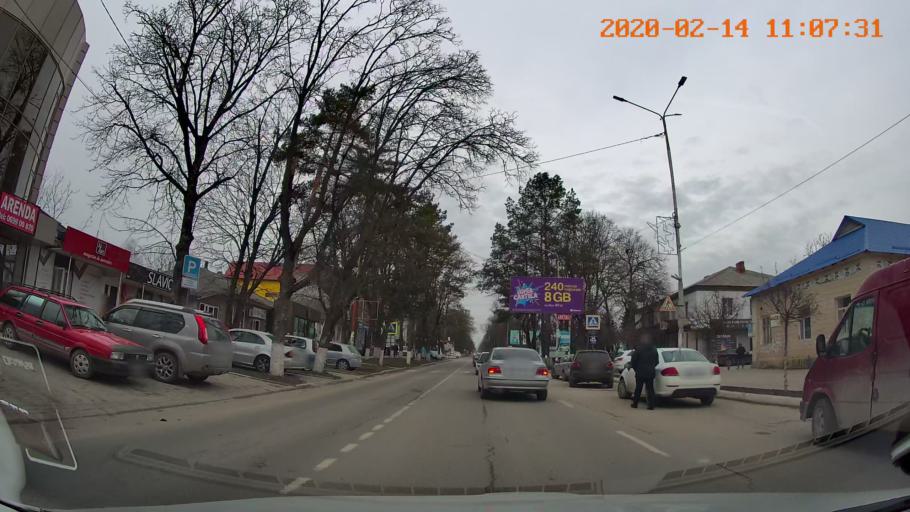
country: MD
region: Raionul Edinet
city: Edinet
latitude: 48.1697
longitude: 27.3057
